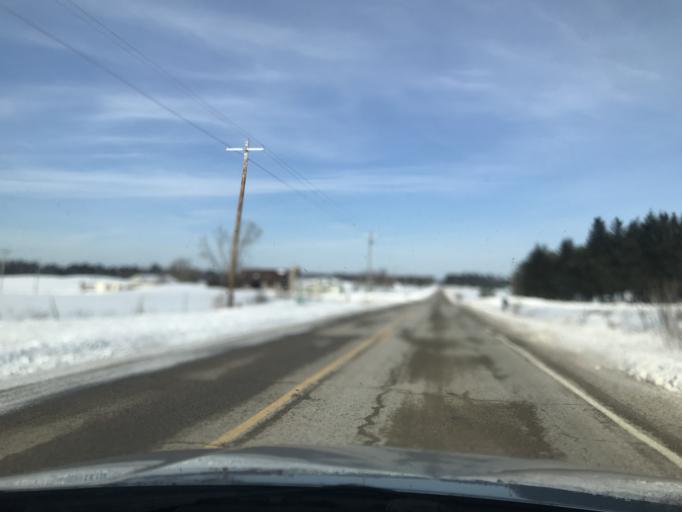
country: US
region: Wisconsin
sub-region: Oconto County
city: Oconto Falls
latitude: 45.1248
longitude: -88.1780
